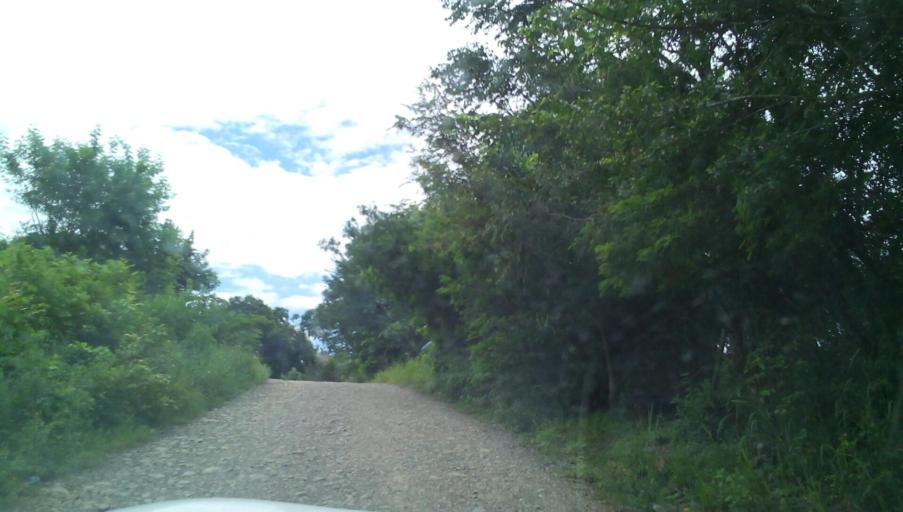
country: MX
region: Veracruz
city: Tepetzintla
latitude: 21.1488
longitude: -97.8562
